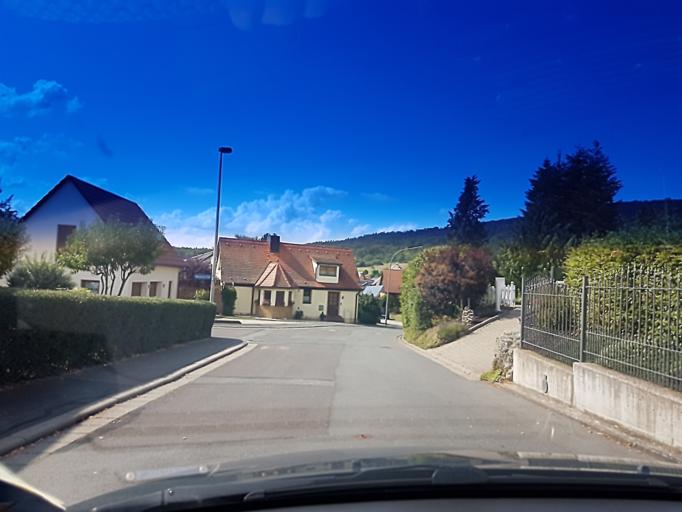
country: DE
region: Bavaria
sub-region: Upper Franconia
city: Litzendorf
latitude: 49.8726
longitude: 11.0475
